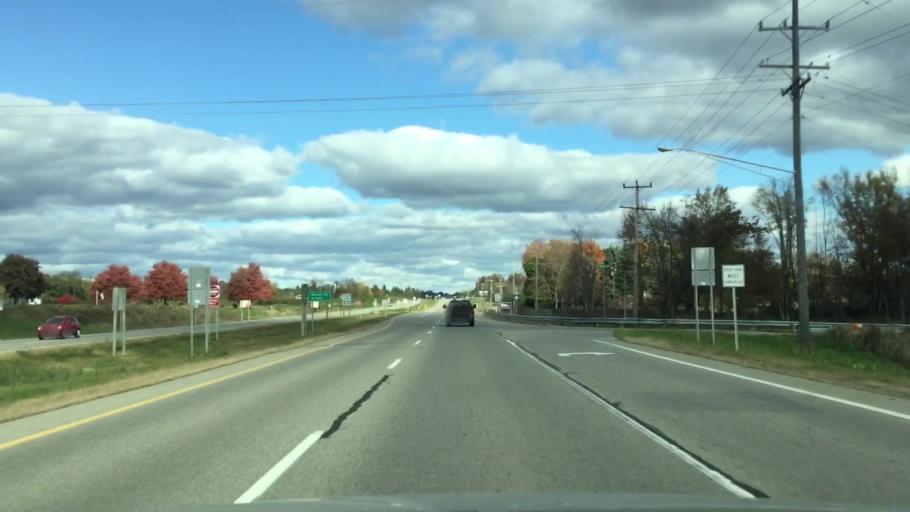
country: US
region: Michigan
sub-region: Lapeer County
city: Lapeer
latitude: 42.9994
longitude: -83.3211
